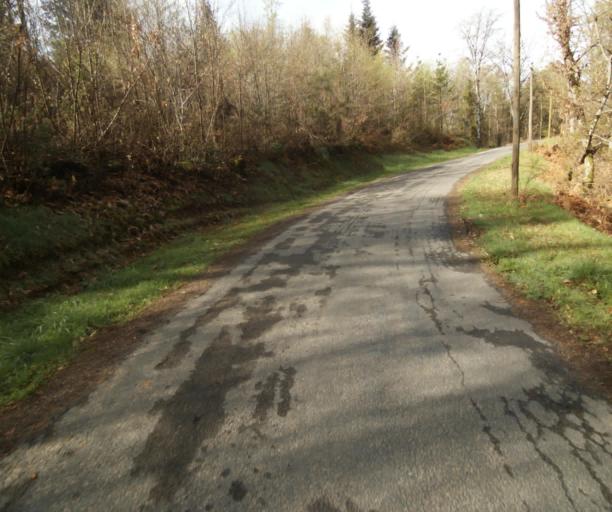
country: FR
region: Limousin
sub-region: Departement de la Correze
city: Laguenne
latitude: 45.2817
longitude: 1.8302
